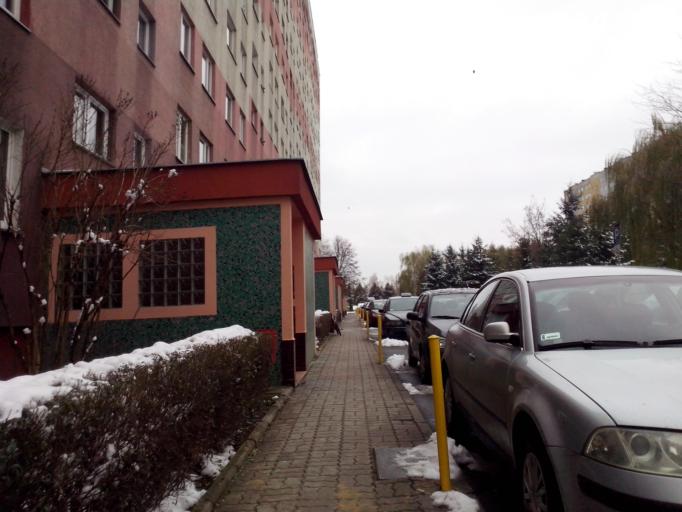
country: PL
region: Subcarpathian Voivodeship
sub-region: Rzeszow
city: Rzeszow
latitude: 50.0222
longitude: 22.0059
